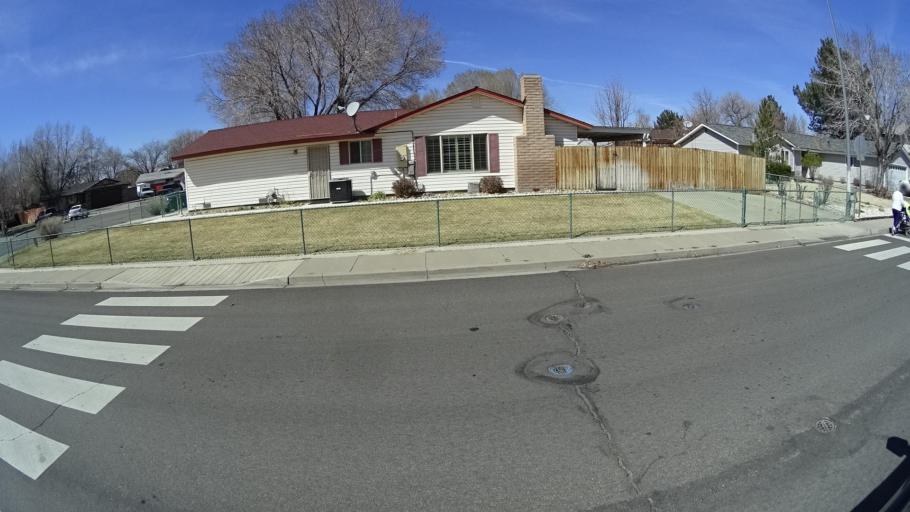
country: US
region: Nevada
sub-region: Washoe County
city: Sparks
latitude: 39.5487
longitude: -119.7318
